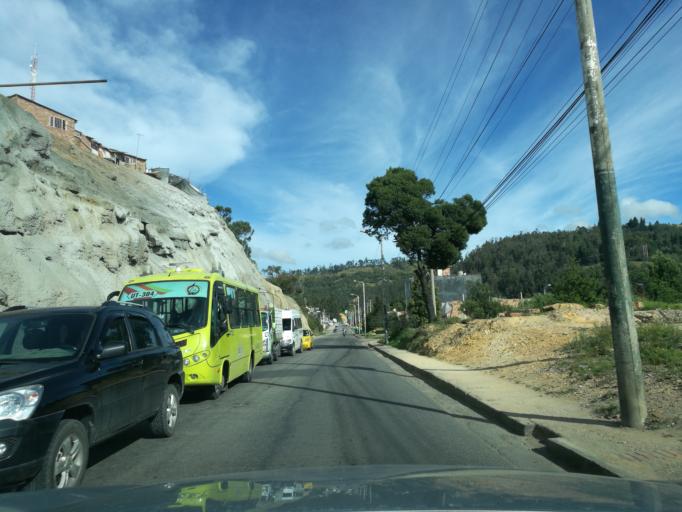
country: CO
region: Boyaca
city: Tunja
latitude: 5.5502
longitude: -73.3604
